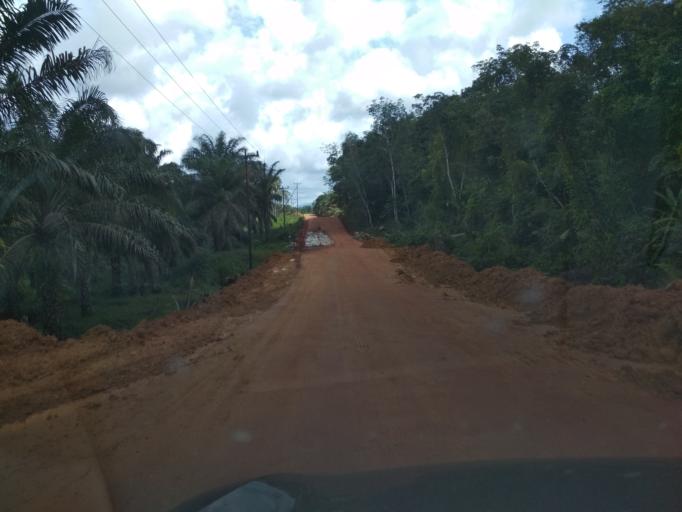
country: ID
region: West Kalimantan
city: Tayan
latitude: 0.5412
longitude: 110.0895
